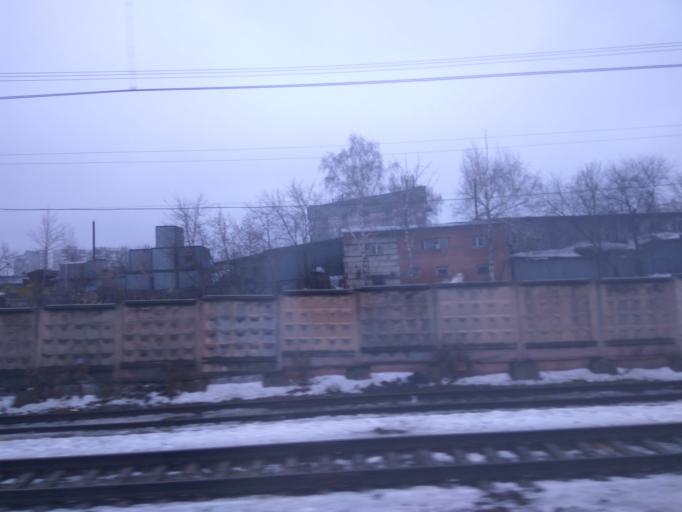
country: RU
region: Moscow
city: Mar'ina Roshcha
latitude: 55.8040
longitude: 37.6235
